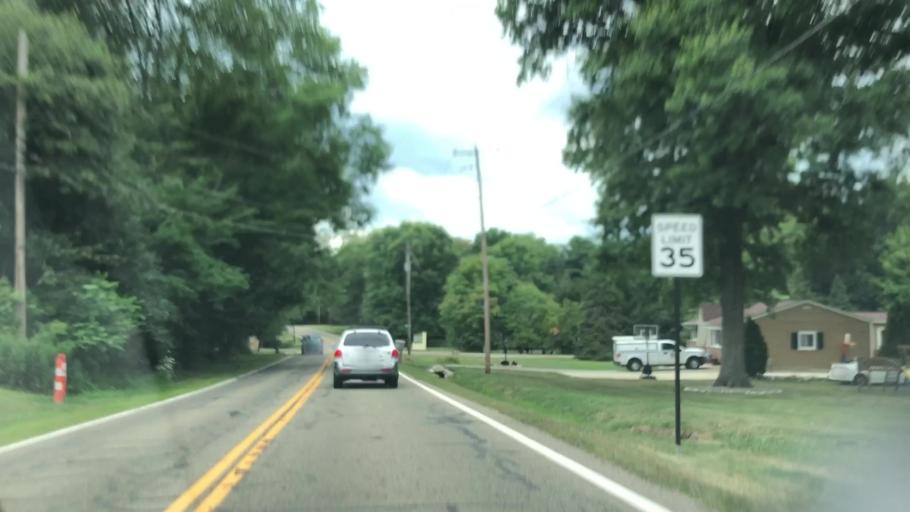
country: US
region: Ohio
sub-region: Summit County
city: Green
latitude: 40.9480
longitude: -81.4852
